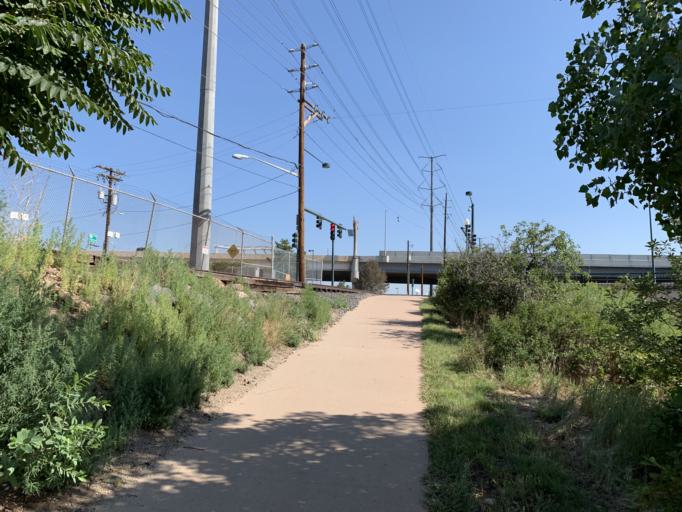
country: US
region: Colorado
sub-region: Denver County
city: Denver
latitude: 39.7395
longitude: -105.0180
